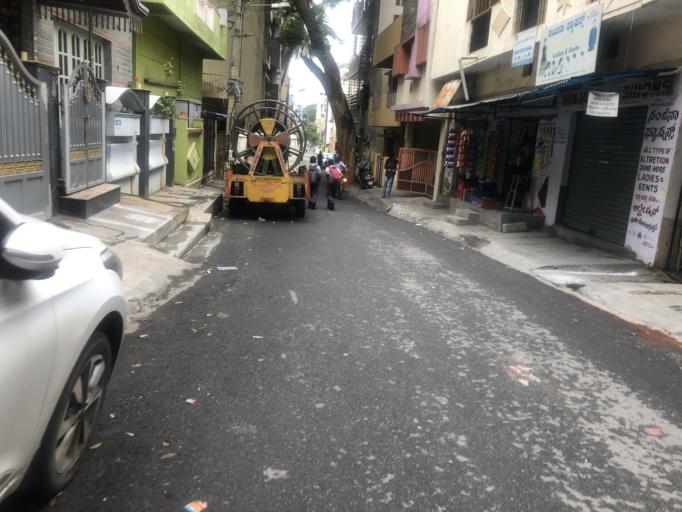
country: IN
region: Karnataka
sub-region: Bangalore Urban
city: Bangalore
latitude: 12.9391
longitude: 77.5522
